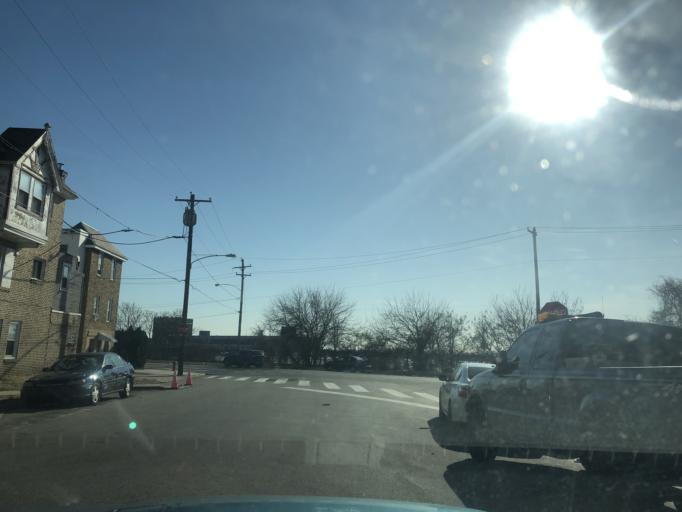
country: US
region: Pennsylvania
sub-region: Montgomery County
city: Bala-Cynwyd
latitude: 39.9842
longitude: -75.2344
